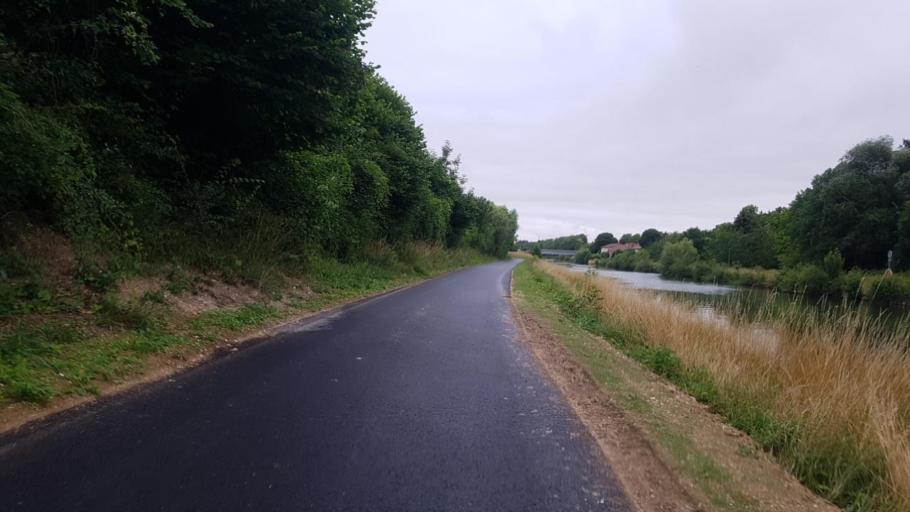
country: FR
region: Champagne-Ardenne
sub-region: Departement de la Marne
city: Vitry-le-Francois
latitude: 48.8095
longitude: 4.5212
